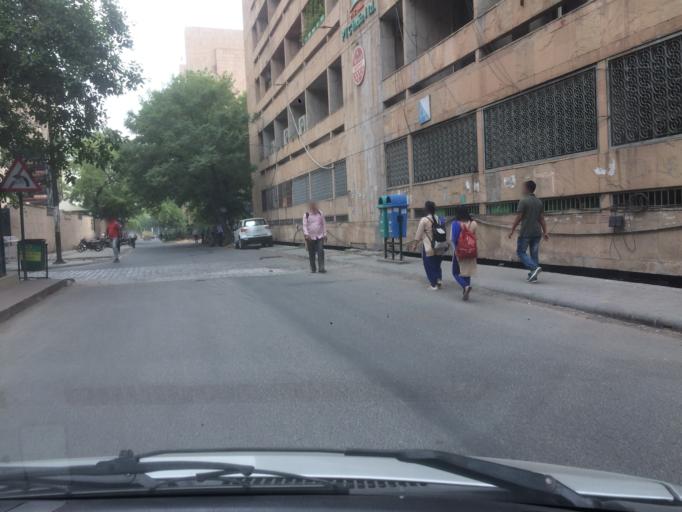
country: IN
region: NCT
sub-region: New Delhi
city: New Delhi
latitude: 28.5678
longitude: 77.1858
